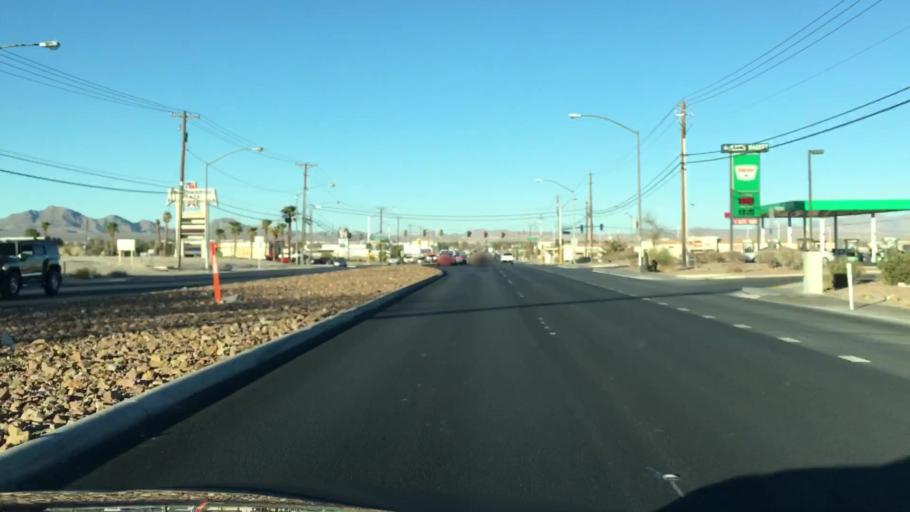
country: US
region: Nevada
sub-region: Clark County
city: Sunrise Manor
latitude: 36.2245
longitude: -115.0817
